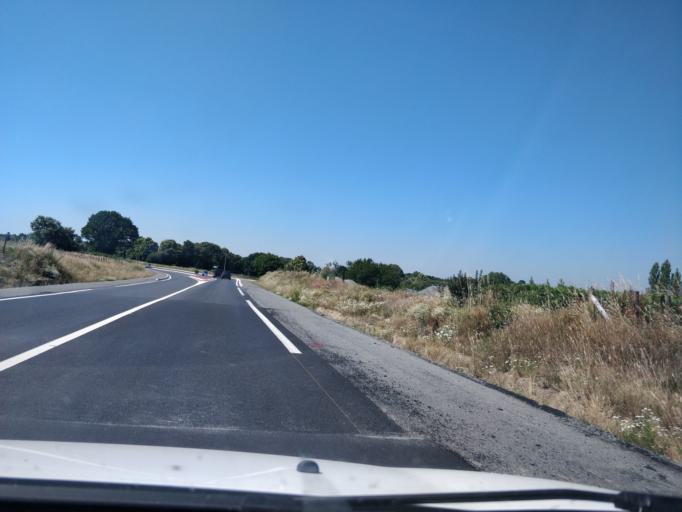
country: FR
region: Brittany
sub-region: Departement d'Ille-et-Vilaine
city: Dol-de-Bretagne
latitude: 48.5257
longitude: -1.7427
